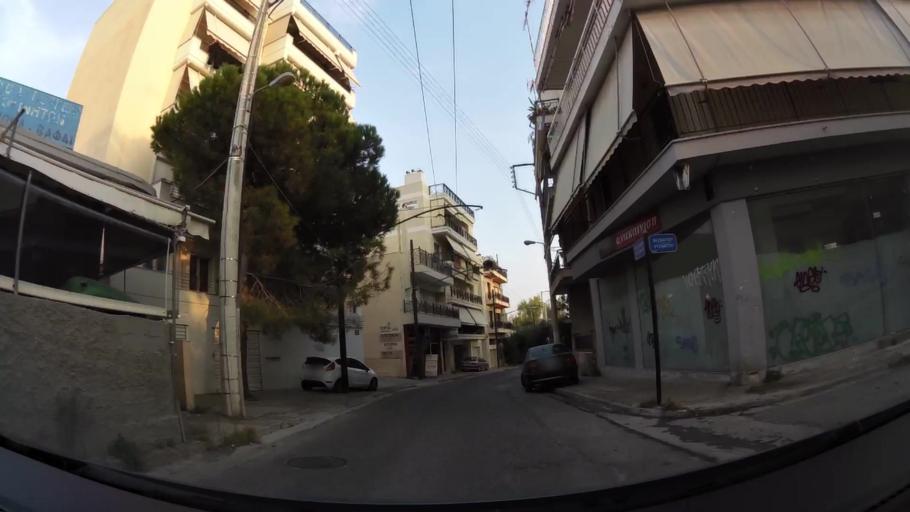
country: GR
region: Attica
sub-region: Nomarchia Athinas
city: Ilion
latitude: 38.0341
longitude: 23.6923
